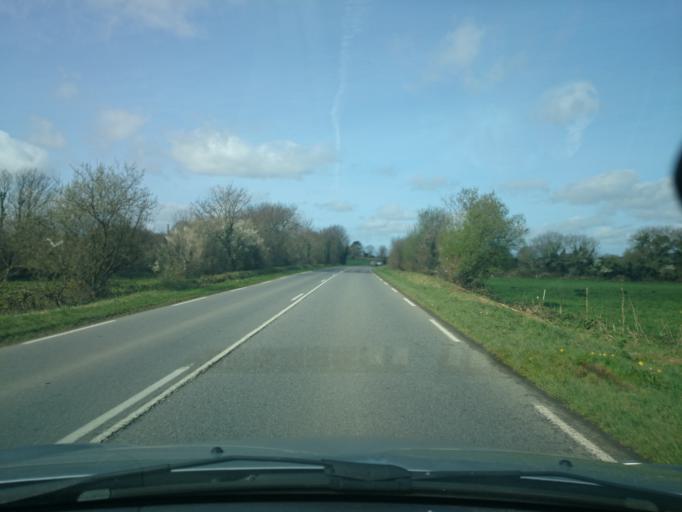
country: FR
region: Brittany
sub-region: Departement du Finistere
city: Gouesnou
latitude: 48.4412
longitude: -4.4468
